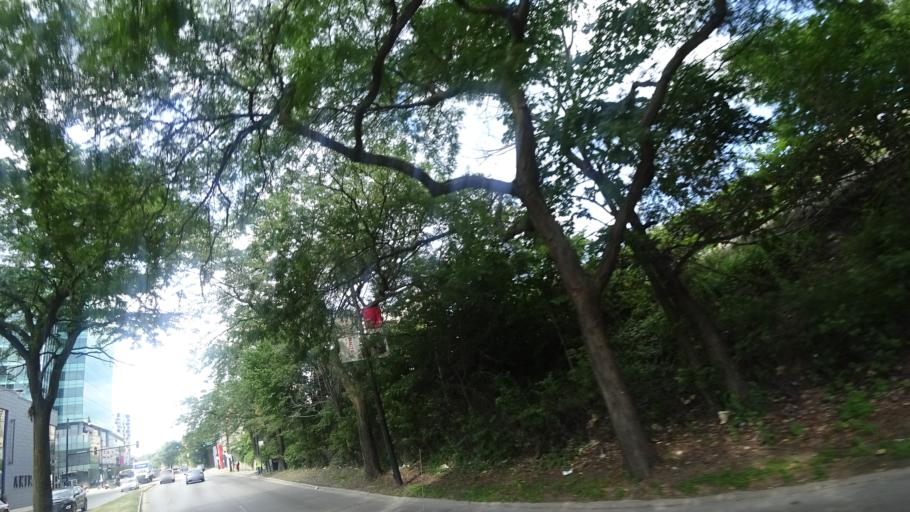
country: US
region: Illinois
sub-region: Cook County
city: Chicago
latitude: 41.7988
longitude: -87.5872
